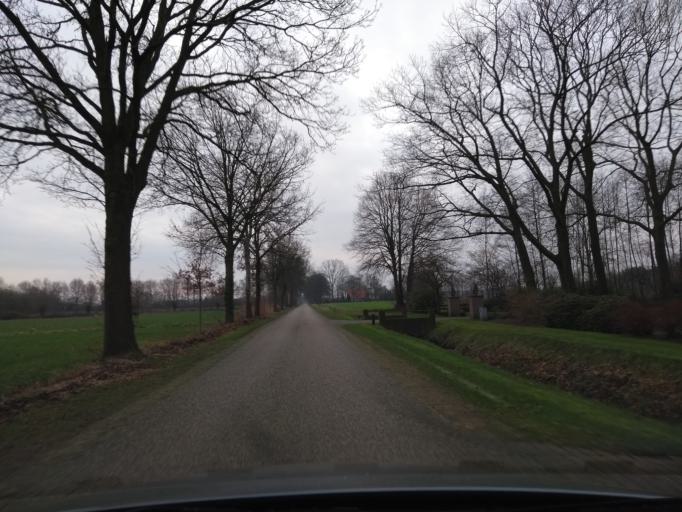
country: NL
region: Overijssel
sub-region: Gemeente Haaksbergen
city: Haaksbergen
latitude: 52.1387
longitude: 6.7508
